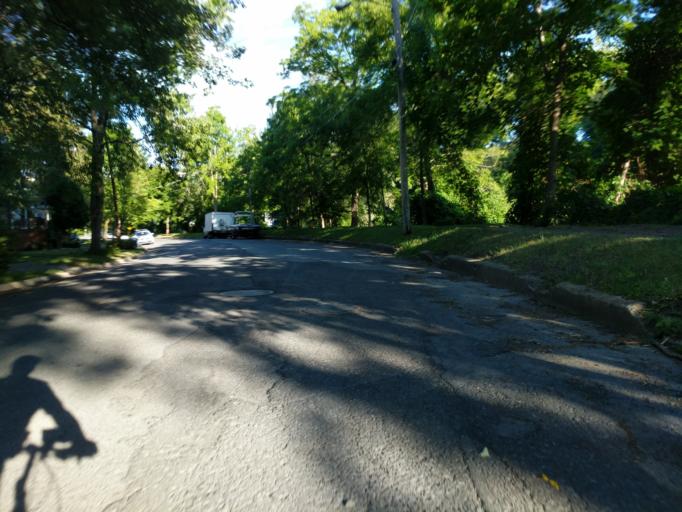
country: US
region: New York
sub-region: Tompkins County
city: Ithaca
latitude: 42.4348
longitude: -76.5058
